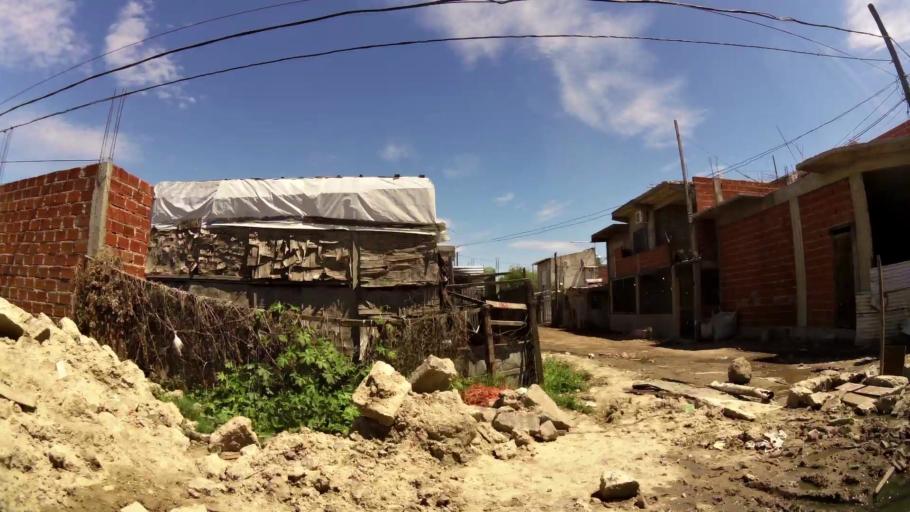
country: AR
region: Buenos Aires
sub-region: Partido de Quilmes
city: Quilmes
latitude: -34.7282
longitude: -58.3166
